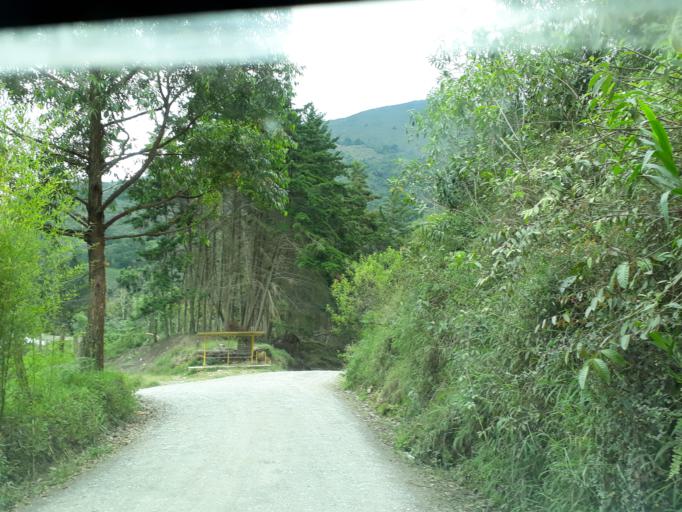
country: CO
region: Cundinamarca
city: Pacho
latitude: 5.2232
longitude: -74.1898
